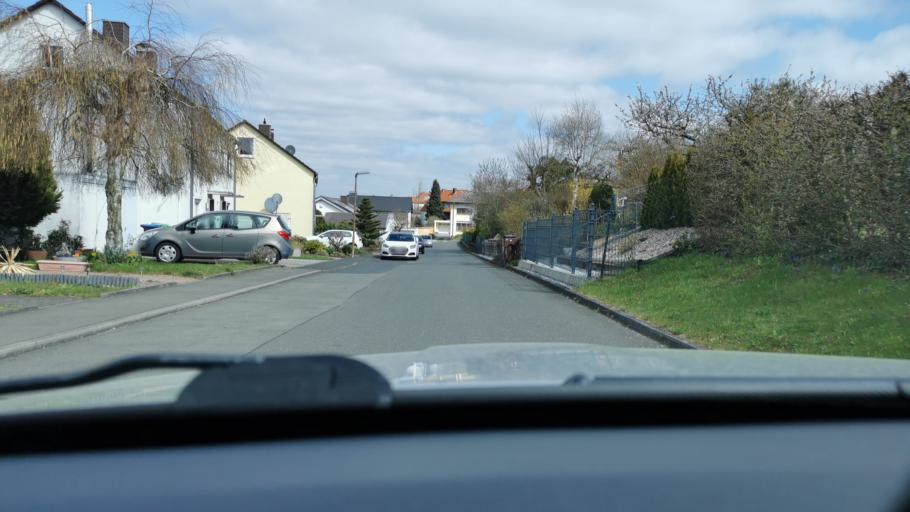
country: DE
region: Hesse
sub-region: Regierungsbezirk Kassel
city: Bad Hersfeld
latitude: 50.8614
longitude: 9.7439
